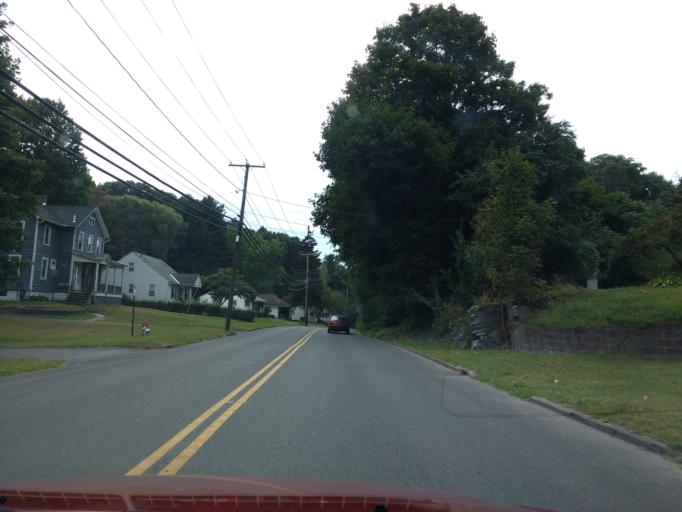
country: US
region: New York
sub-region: Ulster County
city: Kingston
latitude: 41.9356
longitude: -73.9859
